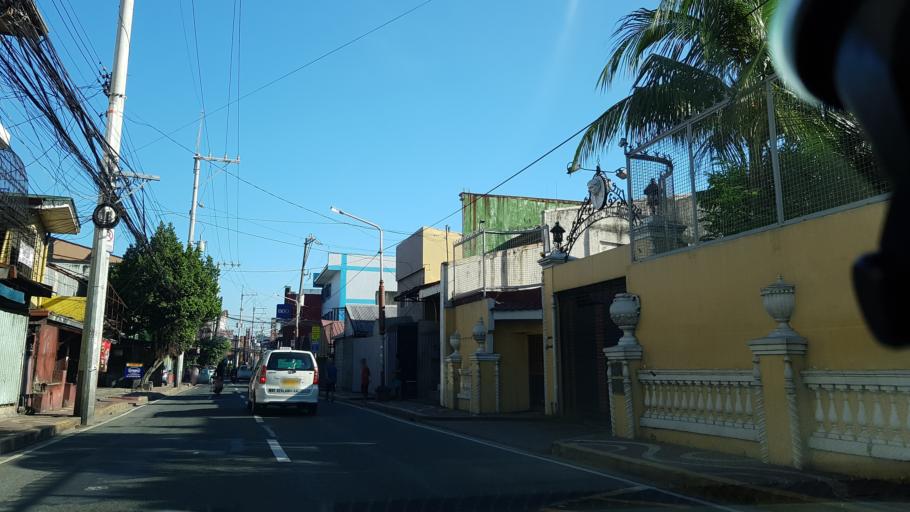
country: PH
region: Calabarzon
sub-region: Province of Rizal
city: Pateros
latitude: 14.5622
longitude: 121.0767
